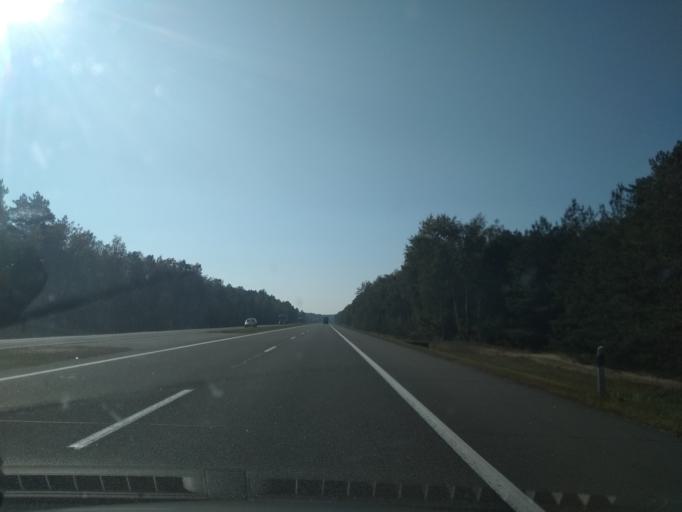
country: BY
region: Brest
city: Antopal'
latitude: 52.3751
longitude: 24.7503
